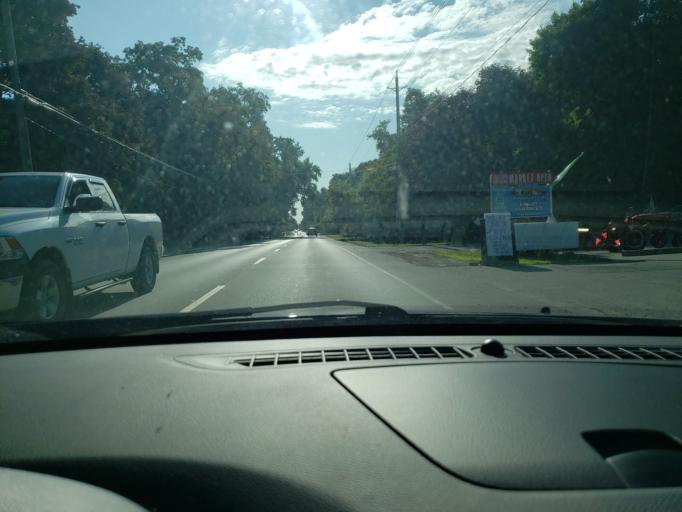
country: CA
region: Ontario
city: Hamilton
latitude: 43.1946
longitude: -79.5950
